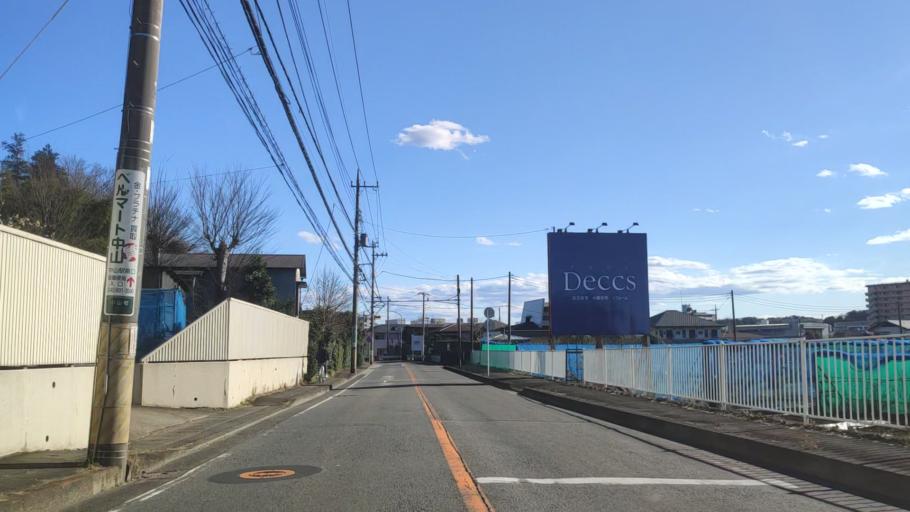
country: JP
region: Tokyo
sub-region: Machida-shi
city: Machida
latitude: 35.5203
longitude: 139.5376
